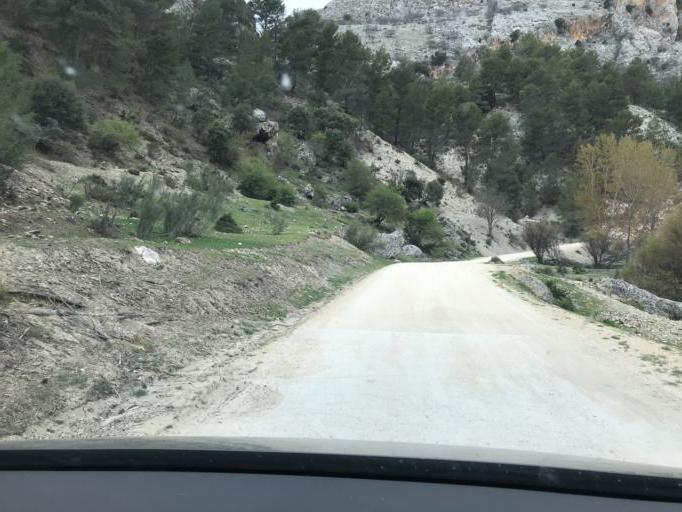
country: ES
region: Andalusia
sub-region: Provincia de Granada
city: Castril
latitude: 37.8511
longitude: -2.7739
